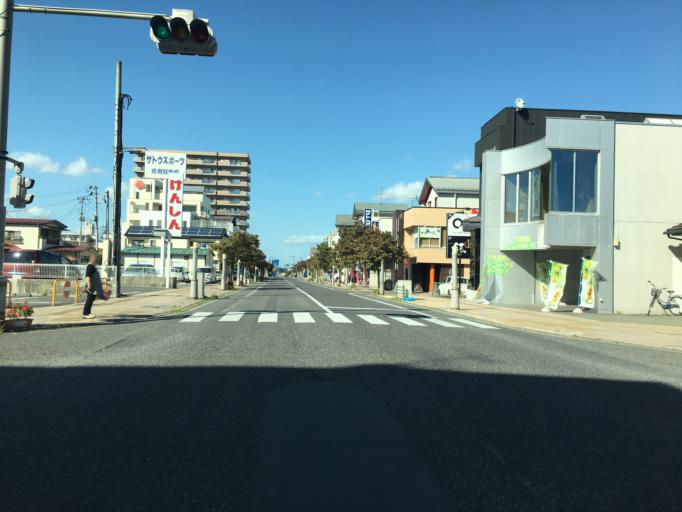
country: JP
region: Fukushima
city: Sukagawa
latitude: 37.2907
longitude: 140.3759
